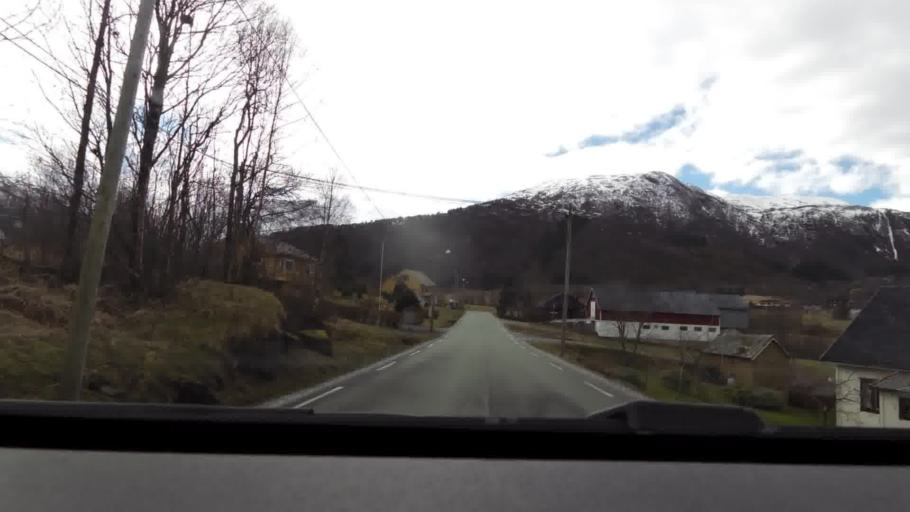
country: NO
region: More og Romsdal
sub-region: Eide
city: Eide
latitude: 62.9118
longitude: 7.5410
